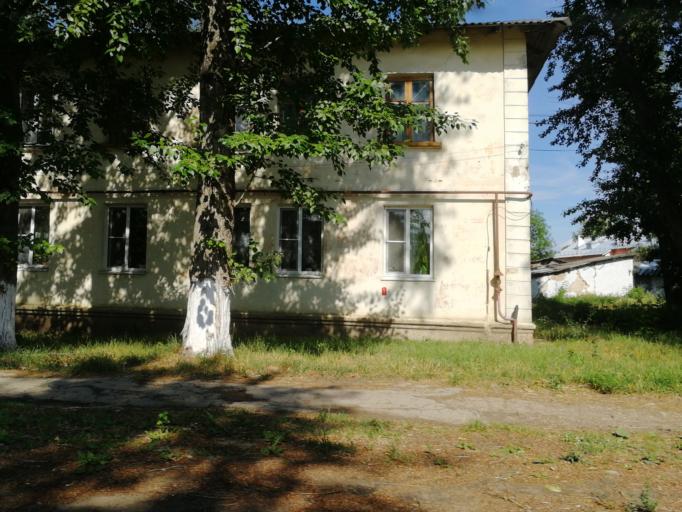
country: RU
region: Tula
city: Bogoroditsk
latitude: 53.7666
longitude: 38.1228
